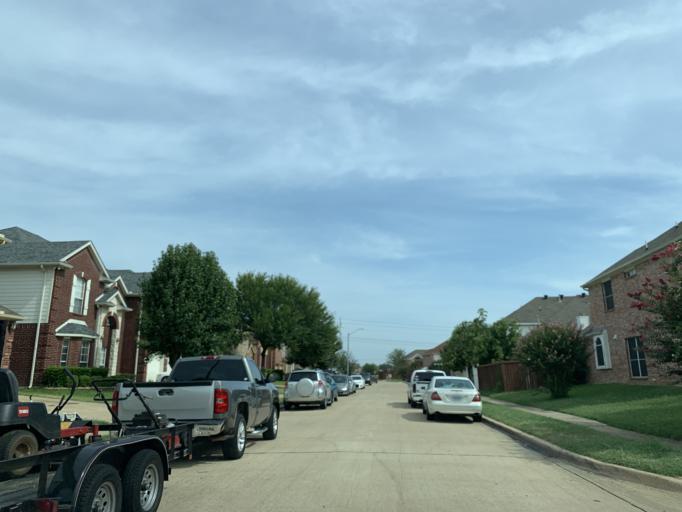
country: US
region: Texas
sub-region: Dallas County
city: Grand Prairie
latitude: 32.6596
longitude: -97.0064
